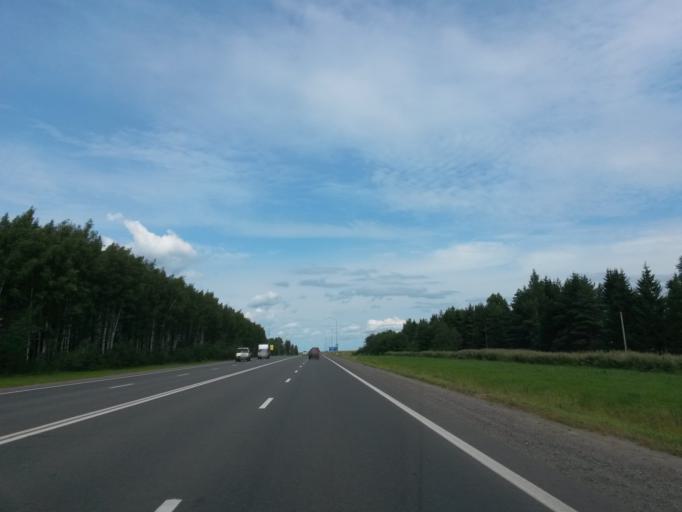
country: RU
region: Jaroslavl
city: Yaroslavl
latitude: 57.7308
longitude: 39.8981
